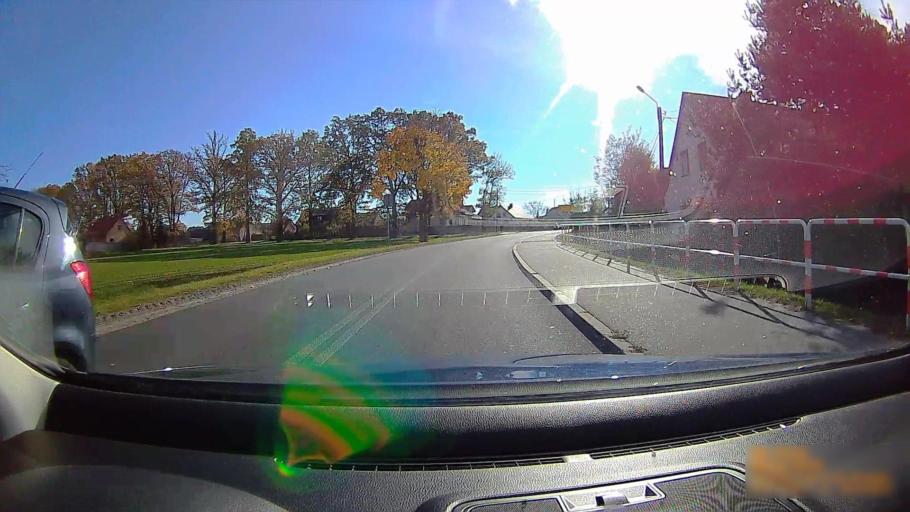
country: PL
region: Greater Poland Voivodeship
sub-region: Powiat ostrzeszowski
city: Doruchow
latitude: 51.3600
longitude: 18.0301
